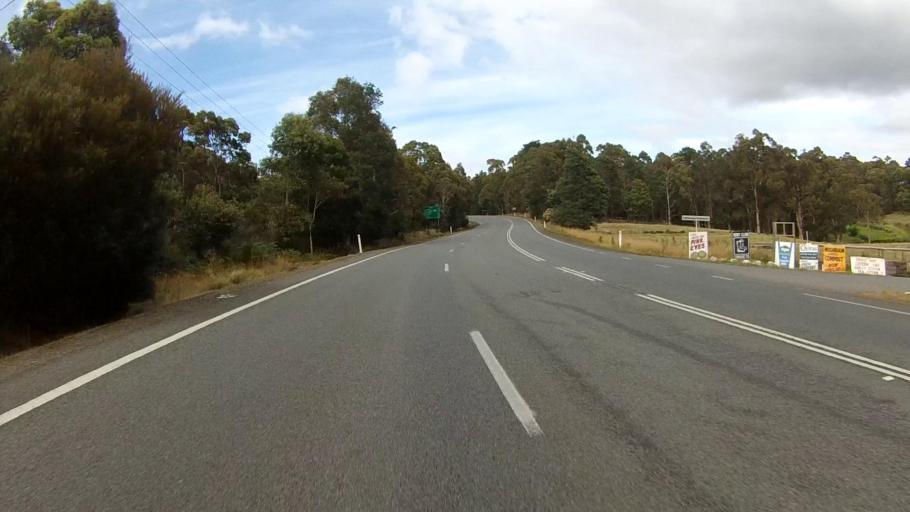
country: AU
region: Tasmania
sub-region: Kingborough
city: Kettering
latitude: -43.1073
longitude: 147.2442
